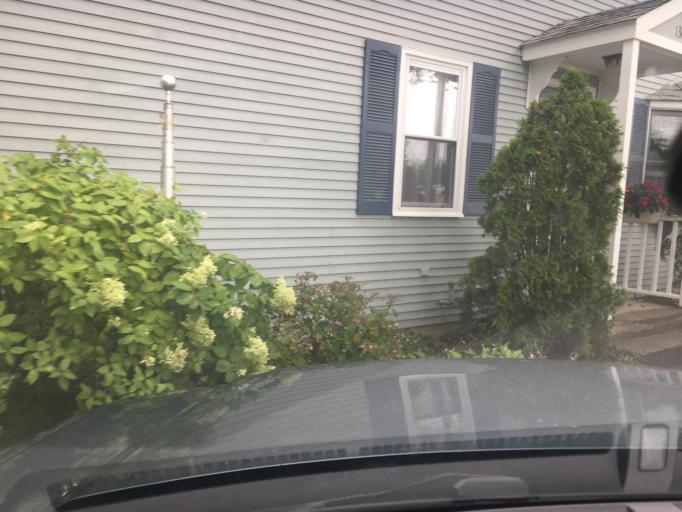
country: US
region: Rhode Island
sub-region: Providence County
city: North Scituate
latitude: 41.8562
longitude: -71.5912
